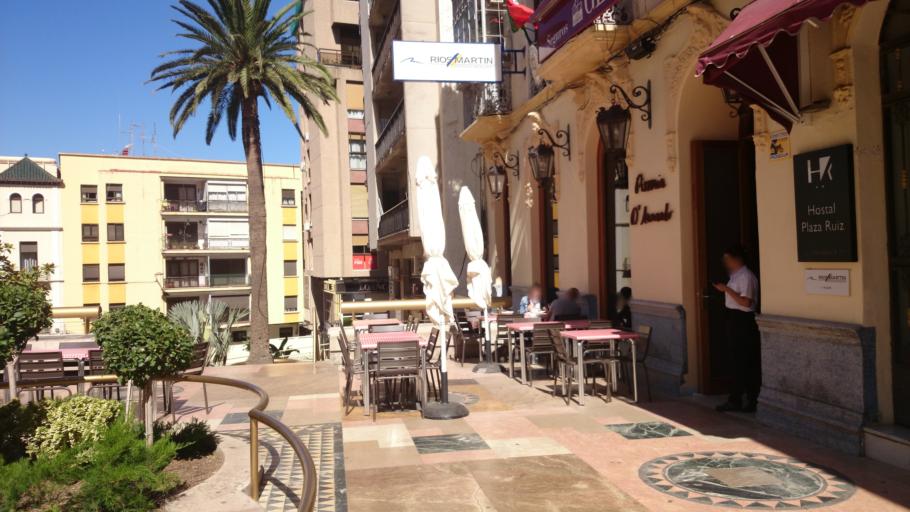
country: ES
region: Ceuta
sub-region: Ceuta
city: Ceuta
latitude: 35.8875
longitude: -5.3103
